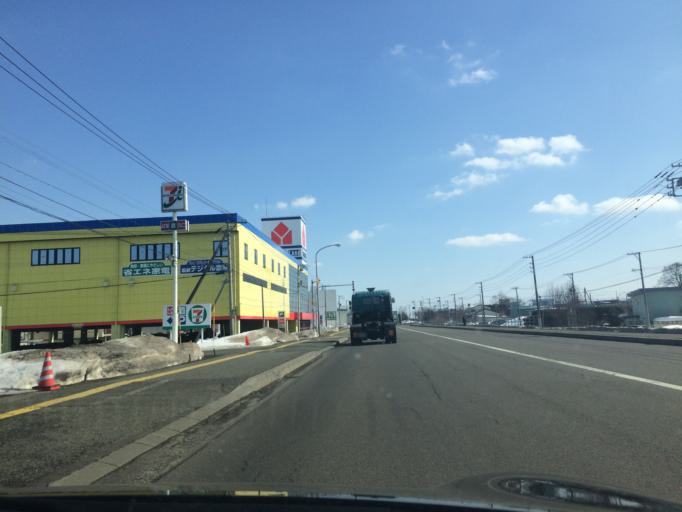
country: JP
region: Hokkaido
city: Chitose
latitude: 42.8296
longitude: 141.6350
